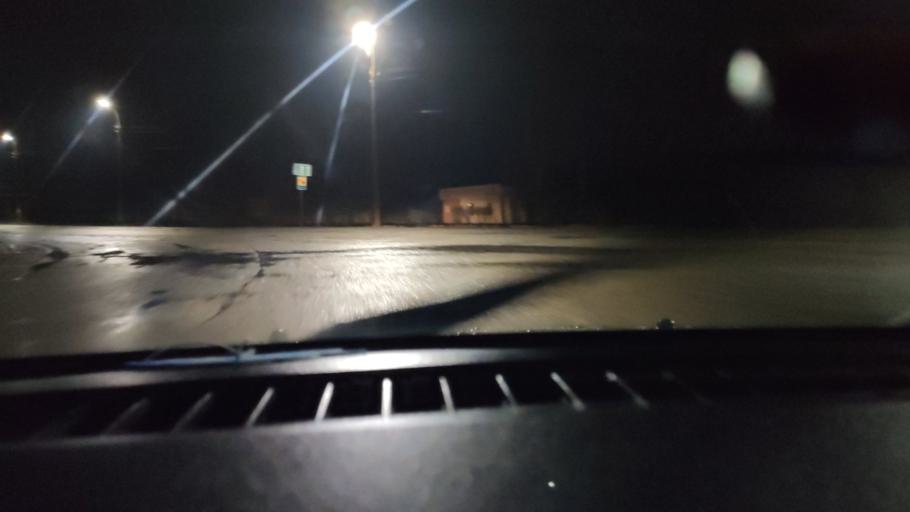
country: RU
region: Udmurtiya
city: Votkinsk
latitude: 57.0330
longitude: 53.9349
